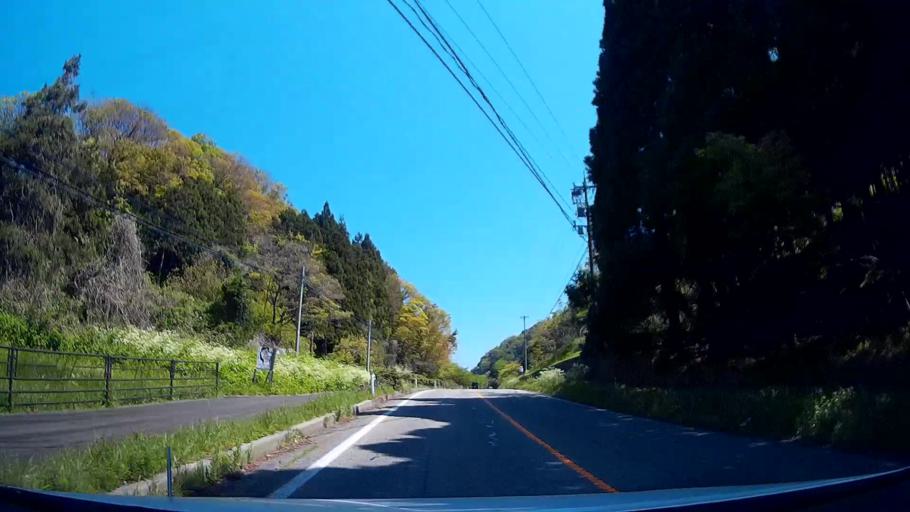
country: JP
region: Ishikawa
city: Nanao
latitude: 37.4117
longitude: 136.9752
